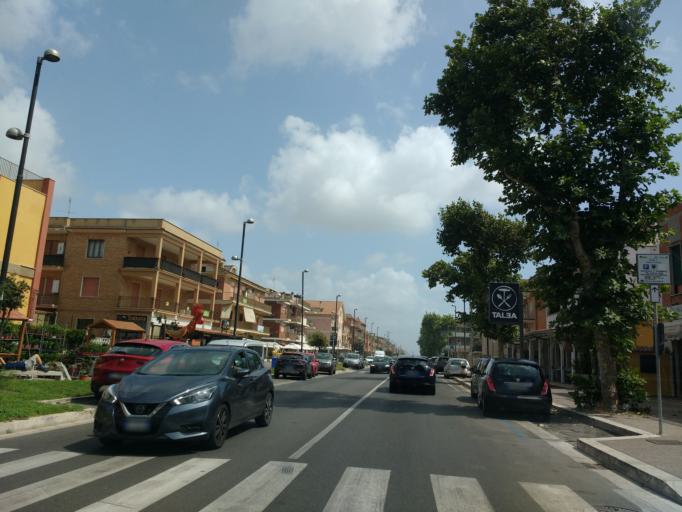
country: IT
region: Latium
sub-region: Citta metropolitana di Roma Capitale
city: Torvaianica
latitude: 41.6203
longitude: 12.4632
